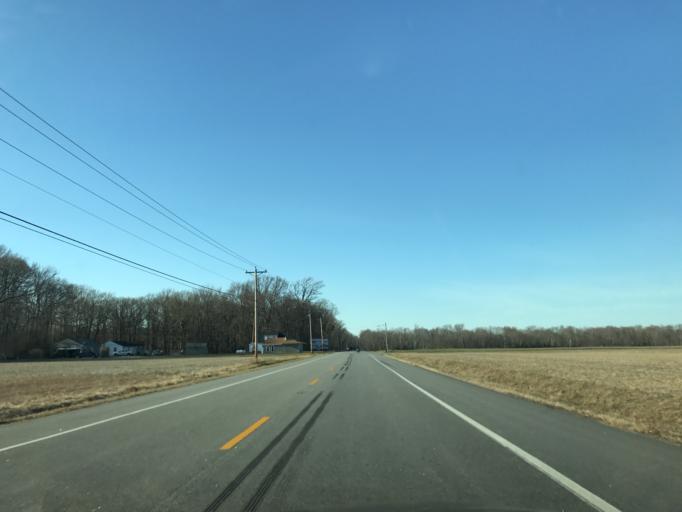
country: US
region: Maryland
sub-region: Queen Anne's County
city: Kingstown
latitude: 39.2253
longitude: -75.8691
